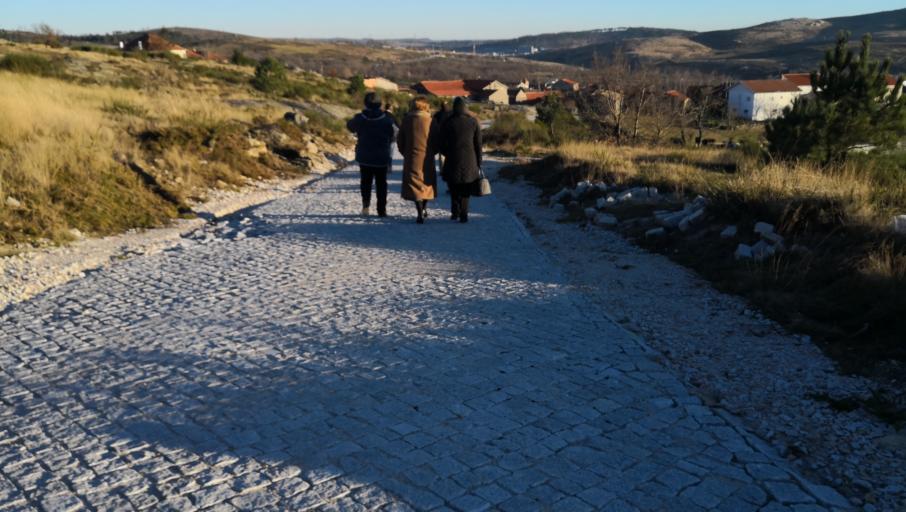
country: PT
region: Vila Real
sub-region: Ribeira de Pena
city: Ribeira de Pena
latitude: 41.5053
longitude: -7.7445
